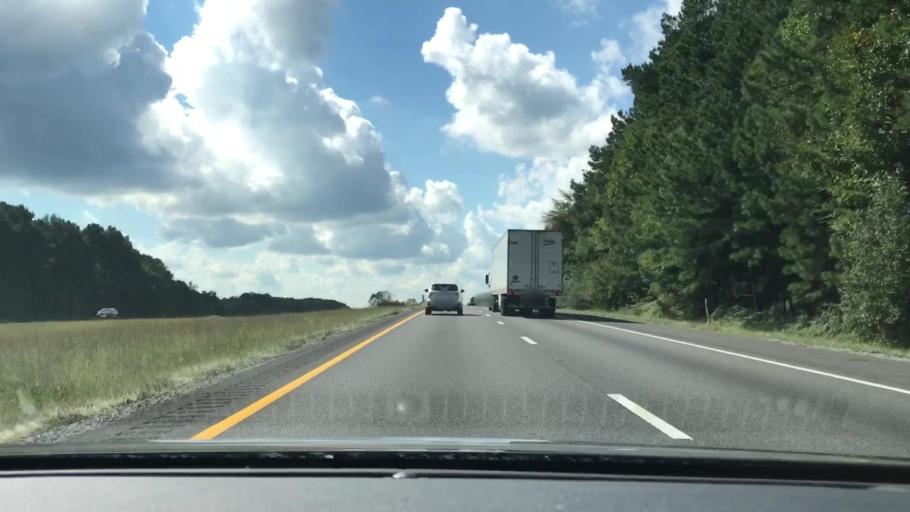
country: US
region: Tennessee
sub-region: Sumner County
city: Millersville
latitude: 36.4236
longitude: -86.7150
